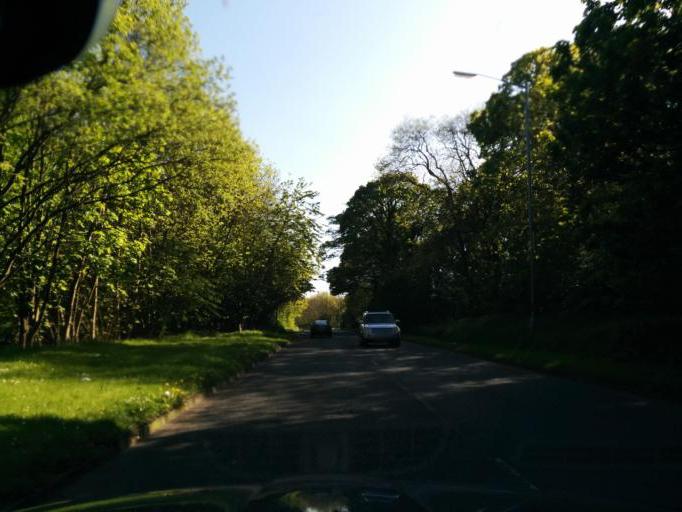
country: GB
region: England
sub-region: Northumberland
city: Cramlington
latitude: 55.0947
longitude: -1.5956
